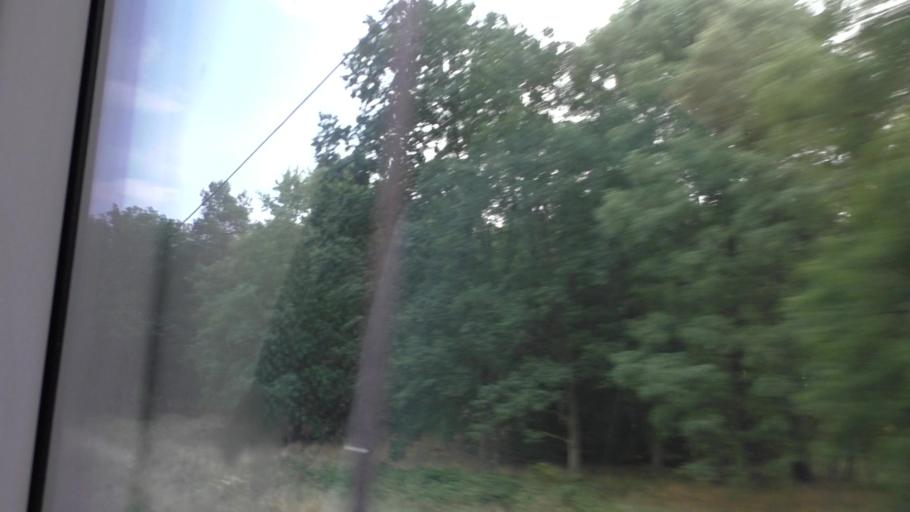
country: DE
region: Brandenburg
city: Storkow
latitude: 52.2634
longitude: 13.8972
